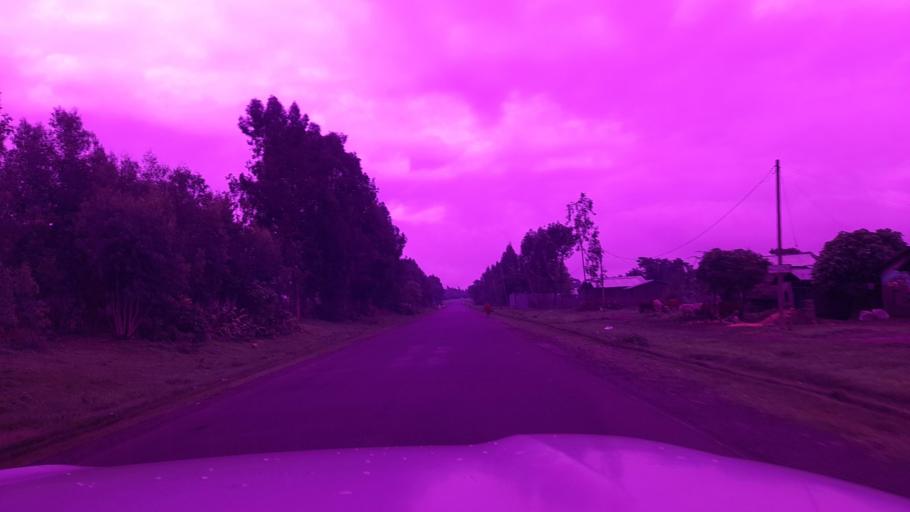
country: ET
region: Oromiya
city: Waliso
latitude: 8.2766
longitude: 37.6818
